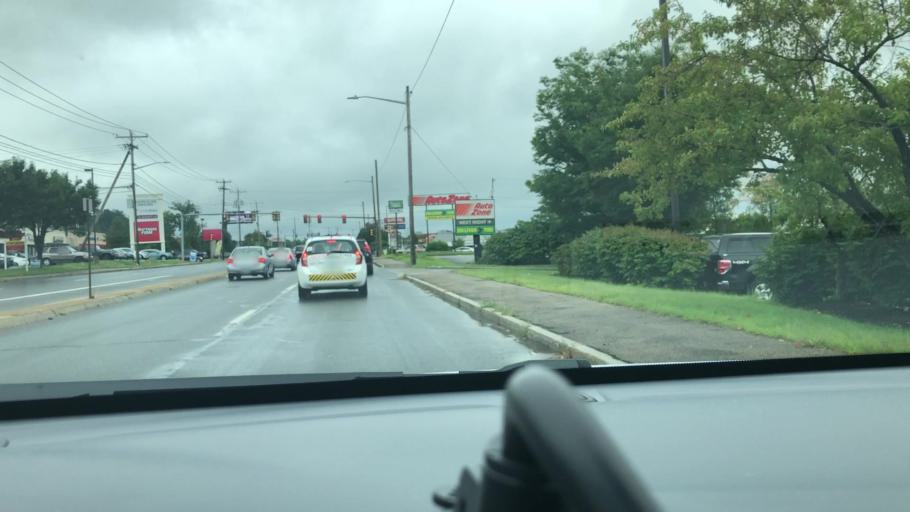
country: US
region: New Hampshire
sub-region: Hillsborough County
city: Manchester
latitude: 42.9633
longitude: -71.4430
